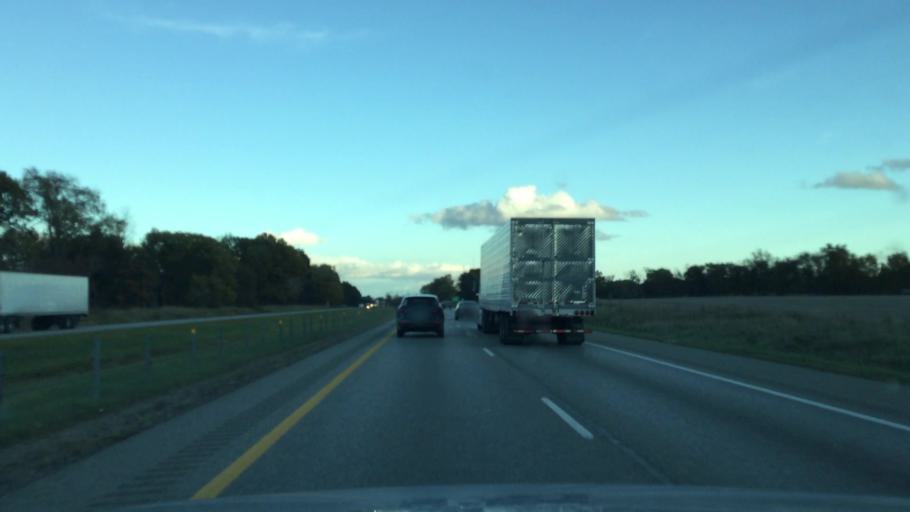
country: US
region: Michigan
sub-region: Calhoun County
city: Lakeview
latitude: 42.2670
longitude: -85.2669
